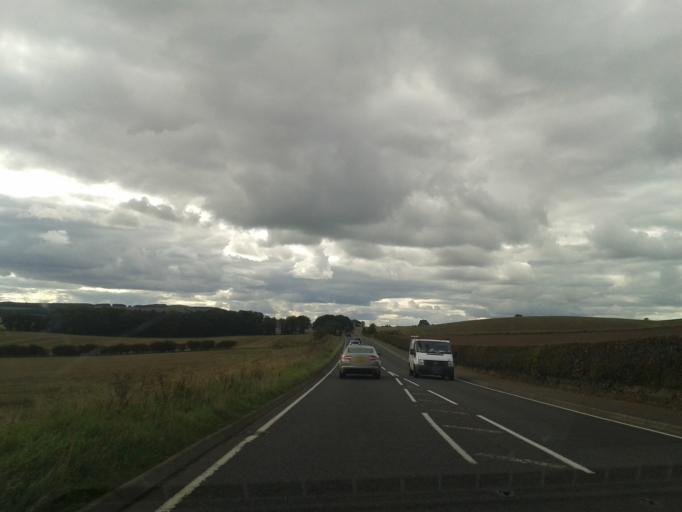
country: GB
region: Scotland
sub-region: Fife
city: Ceres
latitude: 56.3368
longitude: -2.9678
